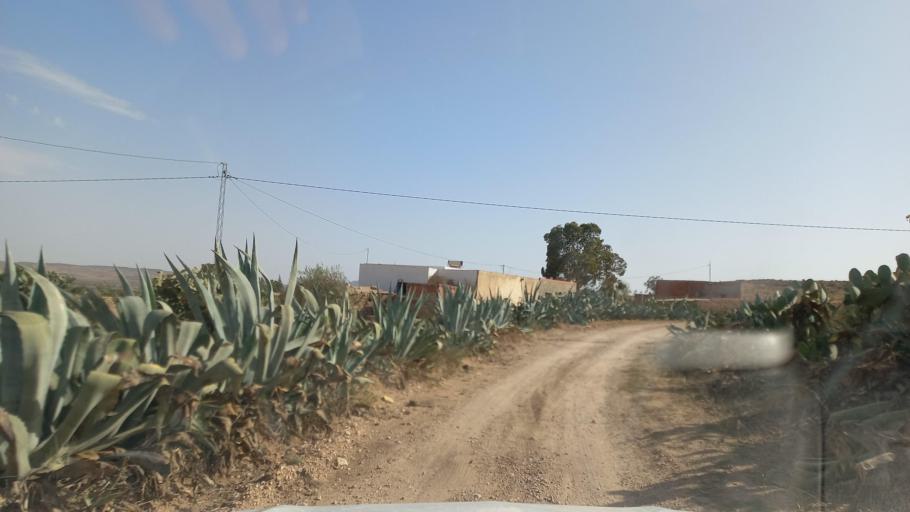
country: TN
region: Al Qasrayn
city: Kasserine
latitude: 35.2557
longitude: 8.9280
